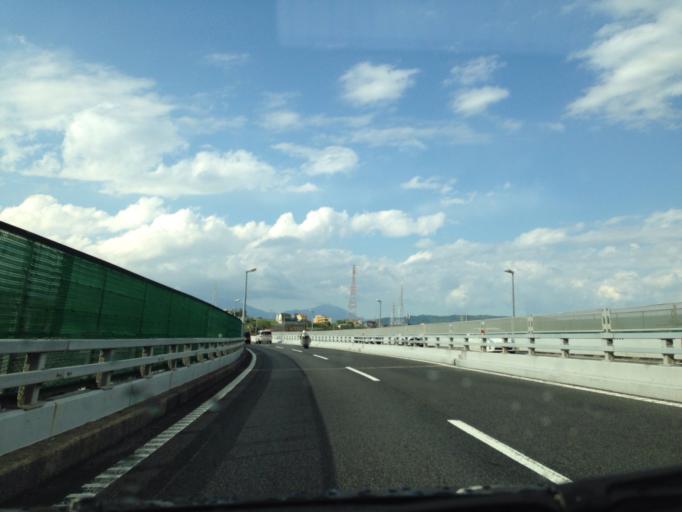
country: JP
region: Kanagawa
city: Odawara
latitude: 35.2690
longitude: 139.1499
